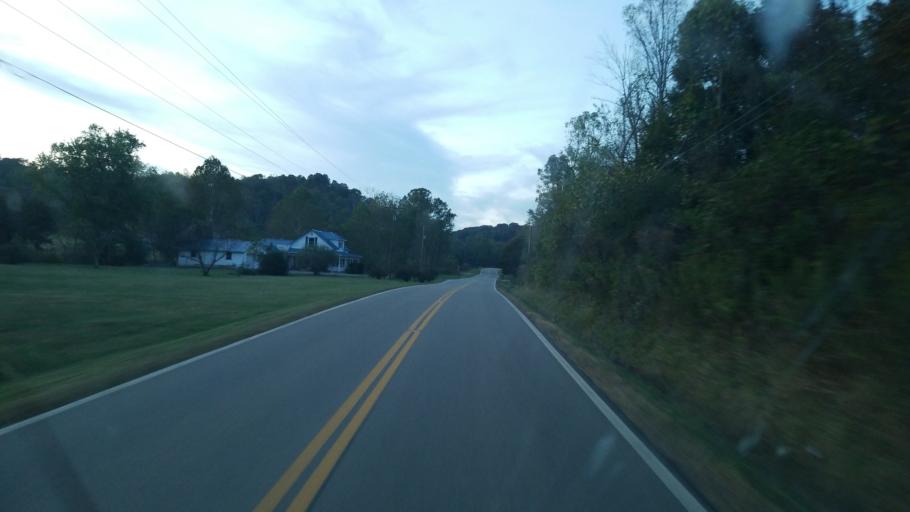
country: US
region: Ohio
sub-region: Meigs County
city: Pomeroy
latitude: 39.0676
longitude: -82.0693
